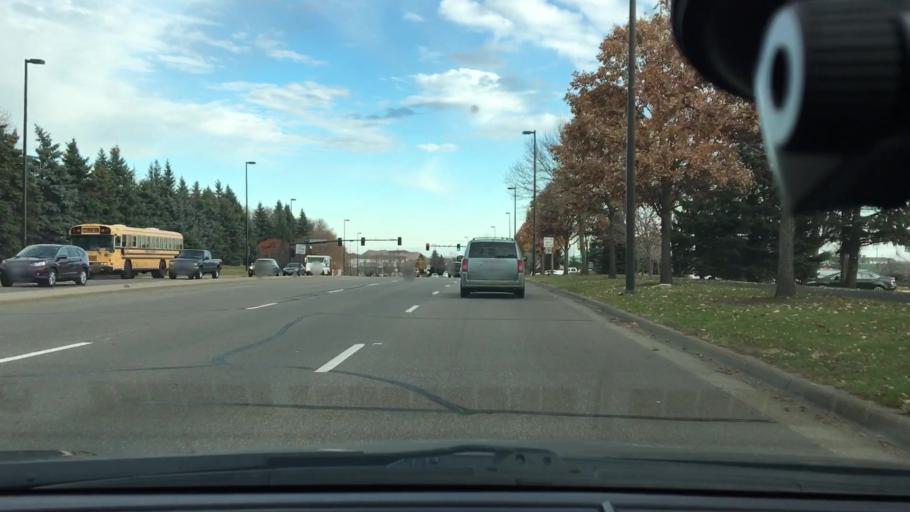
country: US
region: Minnesota
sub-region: Hennepin County
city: Maple Grove
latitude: 45.1044
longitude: -93.4465
